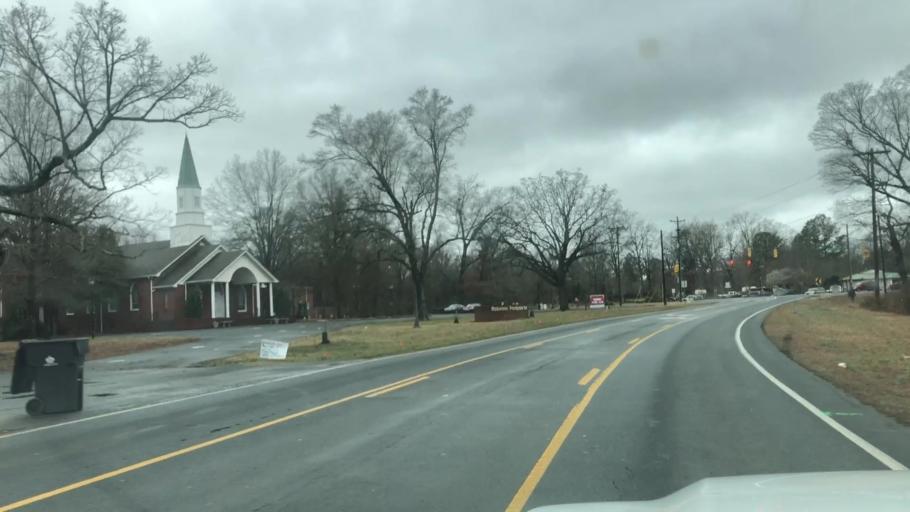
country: US
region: North Carolina
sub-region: Mecklenburg County
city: Mint Hill
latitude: 35.2376
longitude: -80.6685
